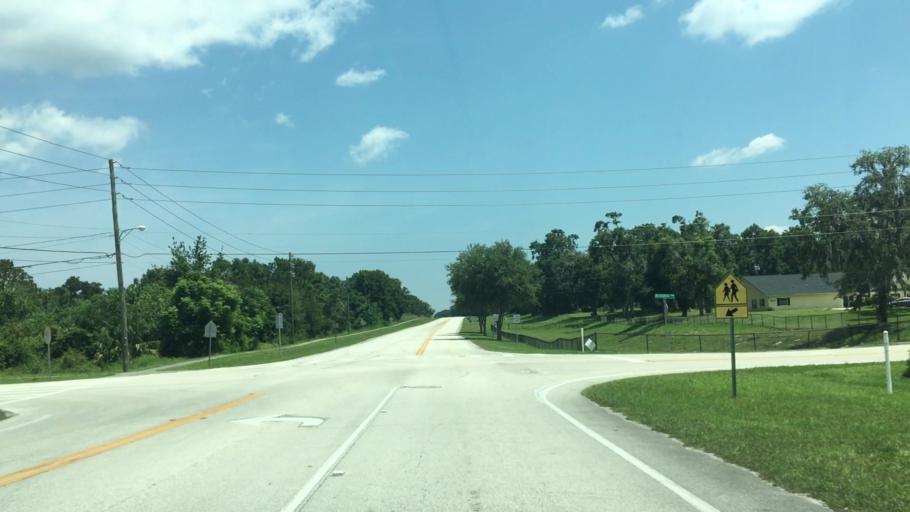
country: US
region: Florida
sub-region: Volusia County
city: Lake Helen
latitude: 28.9700
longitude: -81.2236
